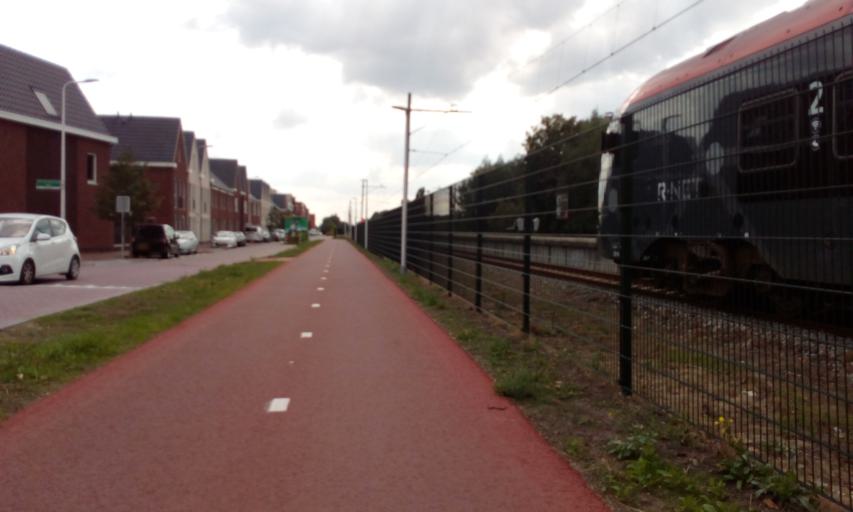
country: NL
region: South Holland
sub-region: Gemeente Waddinxveen
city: Waddinxveen
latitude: 52.0441
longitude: 4.6501
